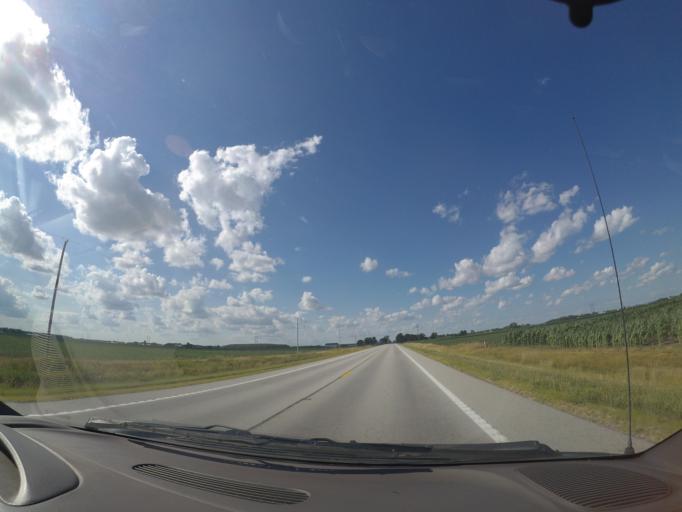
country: US
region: Ohio
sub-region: Wood County
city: Pemberville
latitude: 41.3590
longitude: -83.4169
